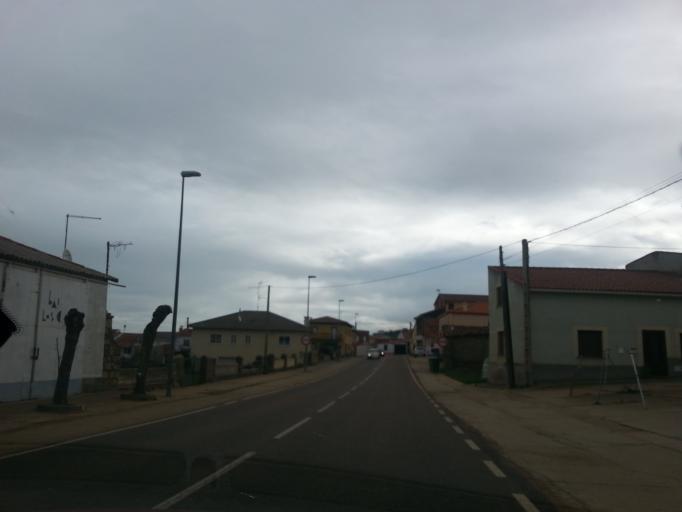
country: ES
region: Castille and Leon
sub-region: Provincia de Salamanca
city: Tamames
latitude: 40.6572
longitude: -6.1094
